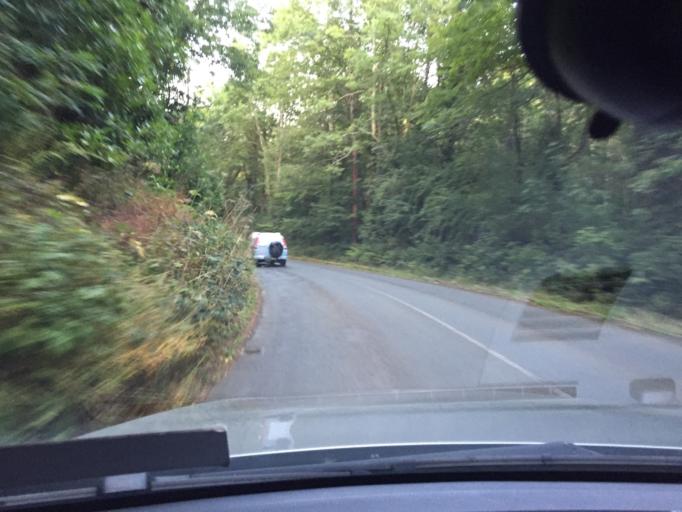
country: IE
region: Leinster
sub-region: Wicklow
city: Enniskerry
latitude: 53.1799
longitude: -6.1725
